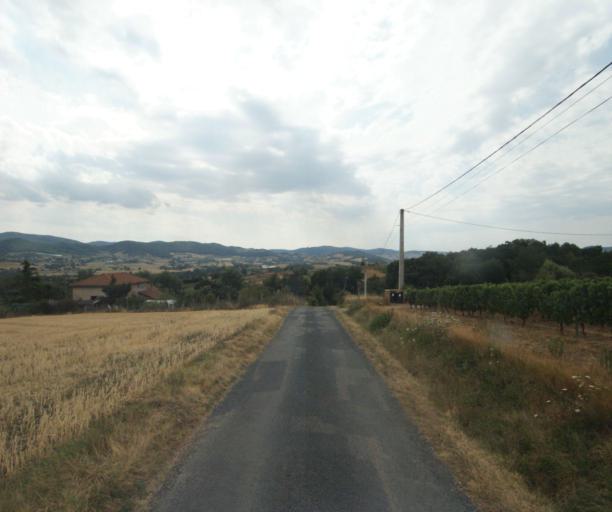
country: FR
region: Rhone-Alpes
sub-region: Departement du Rhone
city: Bully
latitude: 45.8704
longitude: 4.5681
